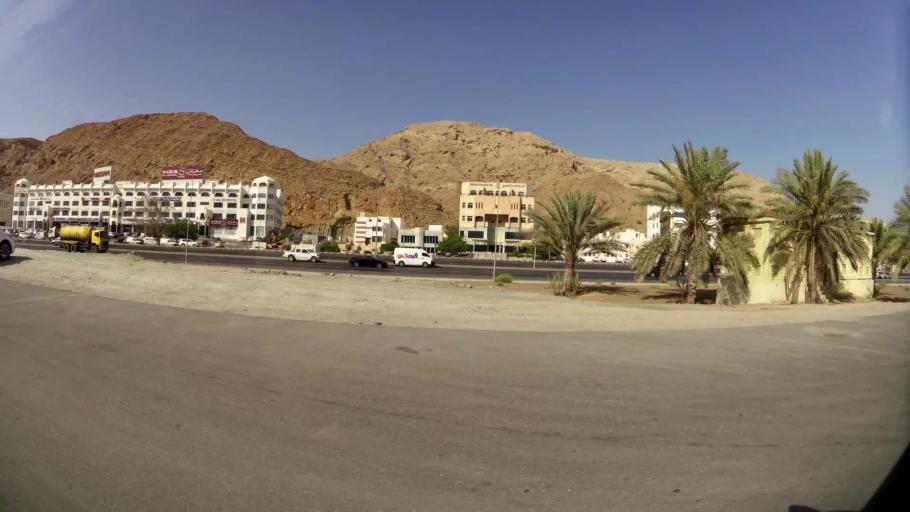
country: OM
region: Muhafazat Masqat
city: Muscat
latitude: 23.5985
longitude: 58.5189
